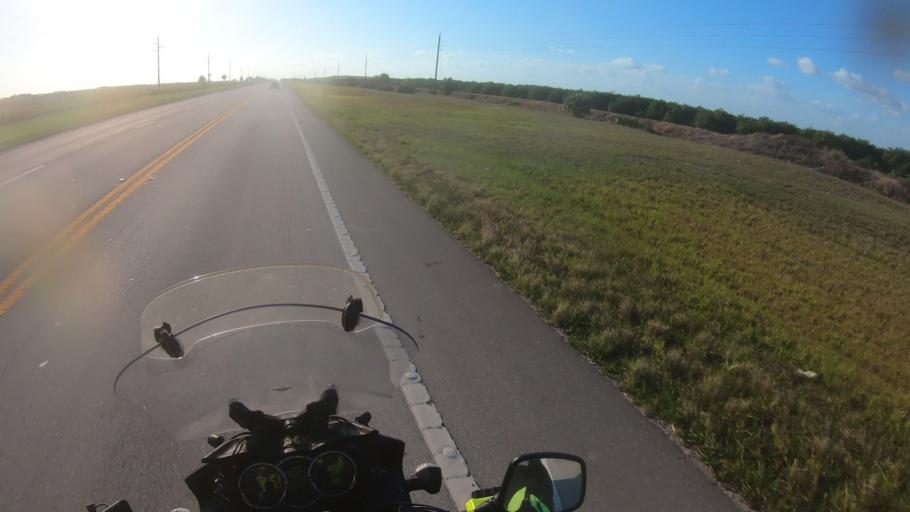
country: US
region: Florida
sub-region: Highlands County
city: Placid Lakes
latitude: 27.2099
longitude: -81.6026
